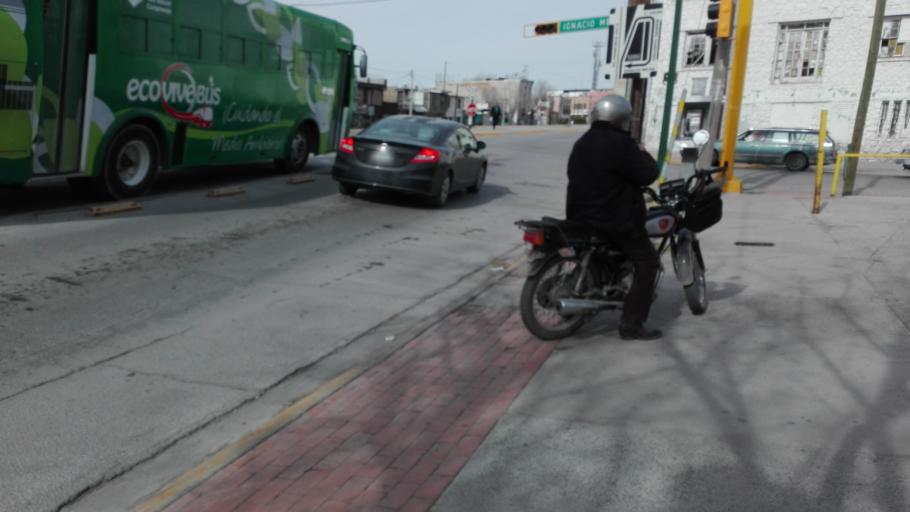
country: MX
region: Chihuahua
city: Ciudad Juarez
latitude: 31.7424
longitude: -106.4840
